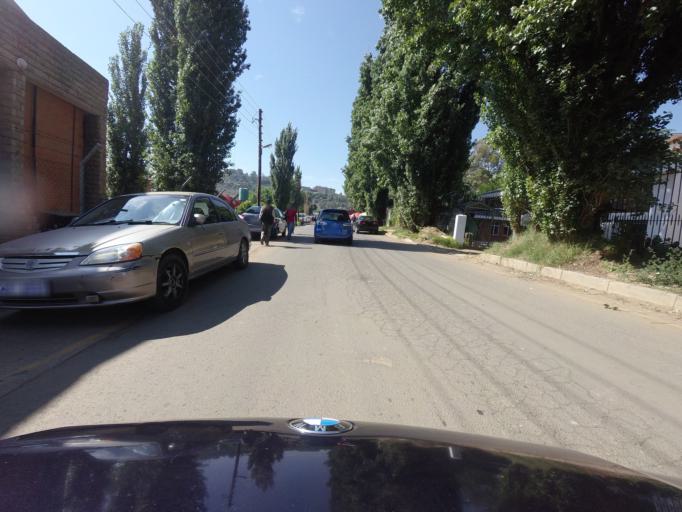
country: LS
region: Maseru
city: Maseru
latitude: -29.3125
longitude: 27.4870
